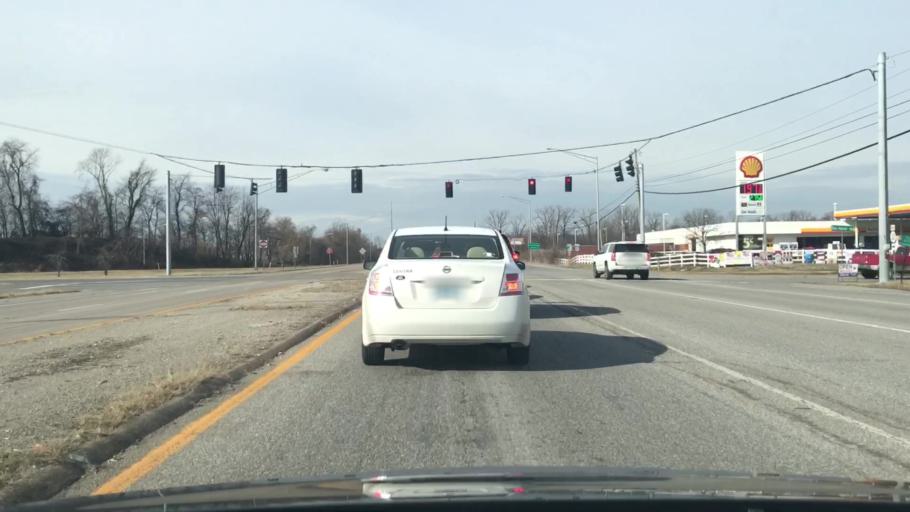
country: US
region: Kentucky
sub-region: Daviess County
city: Owensboro
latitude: 37.7749
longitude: -87.1650
